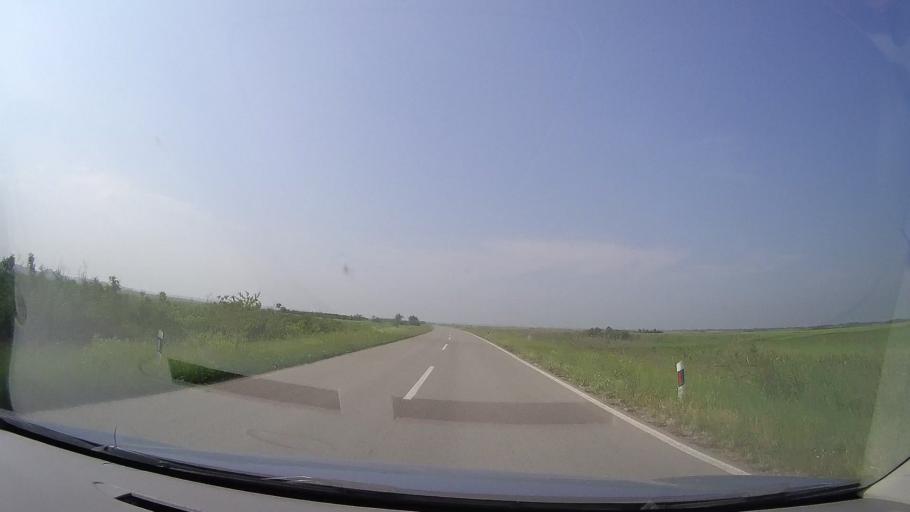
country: RS
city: Jasa Tomic
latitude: 45.4273
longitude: 20.8379
